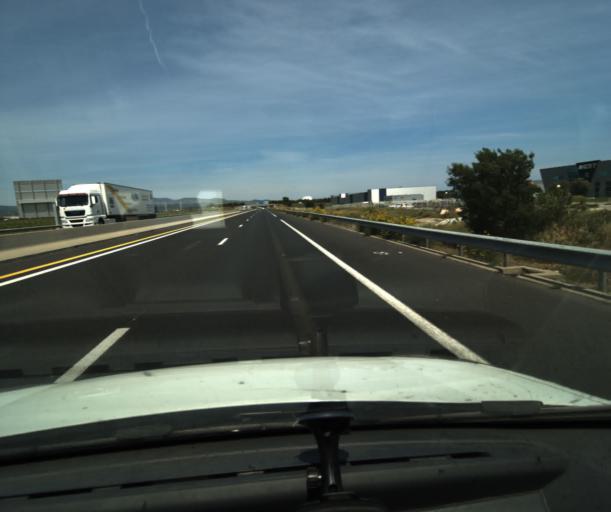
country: FR
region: Languedoc-Roussillon
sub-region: Departement des Pyrenees-Orientales
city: Rivesaltes
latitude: 42.7763
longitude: 2.8940
